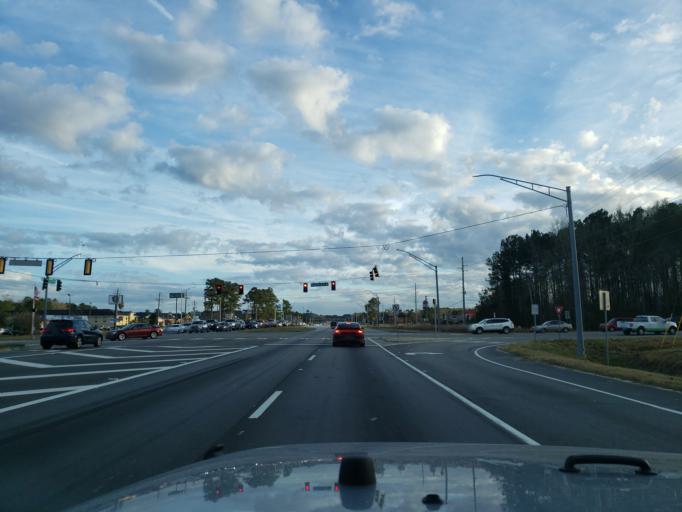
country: US
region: Georgia
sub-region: Chatham County
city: Port Wentworth
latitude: 32.1990
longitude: -81.1979
